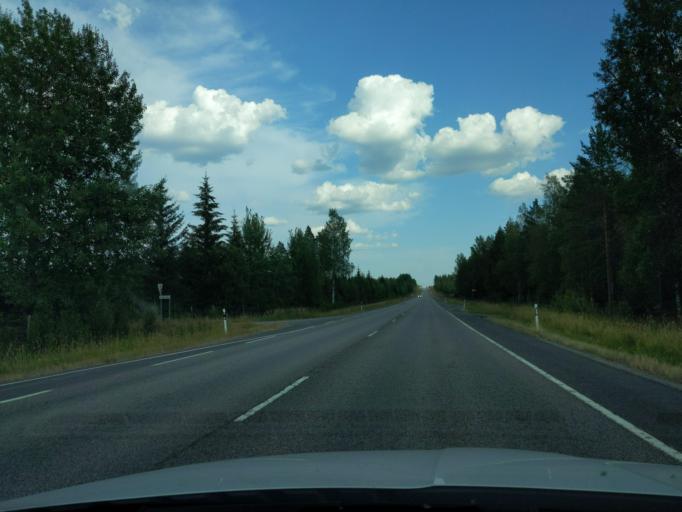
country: FI
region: Paijanne Tavastia
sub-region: Lahti
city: Hollola
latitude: 60.9938
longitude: 25.3681
